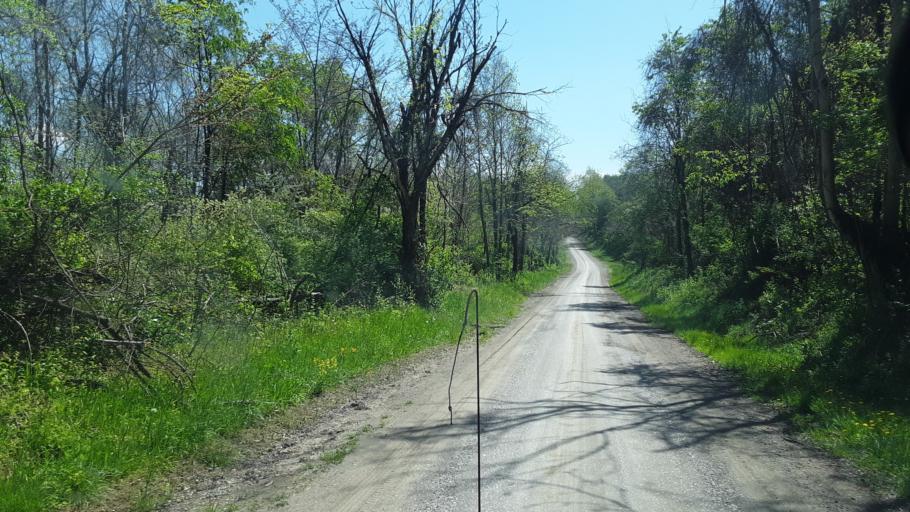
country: US
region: Ohio
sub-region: Noble County
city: Caldwell
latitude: 39.7723
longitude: -81.6138
